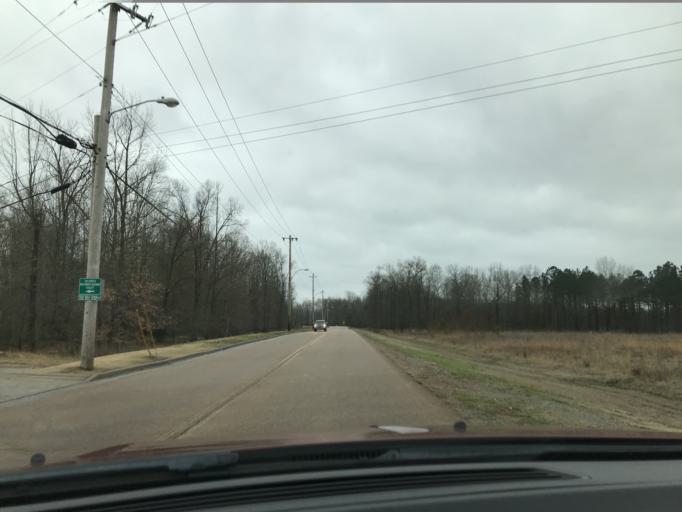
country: US
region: Tennessee
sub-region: Shelby County
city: Collierville
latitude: 35.0940
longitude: -89.7152
